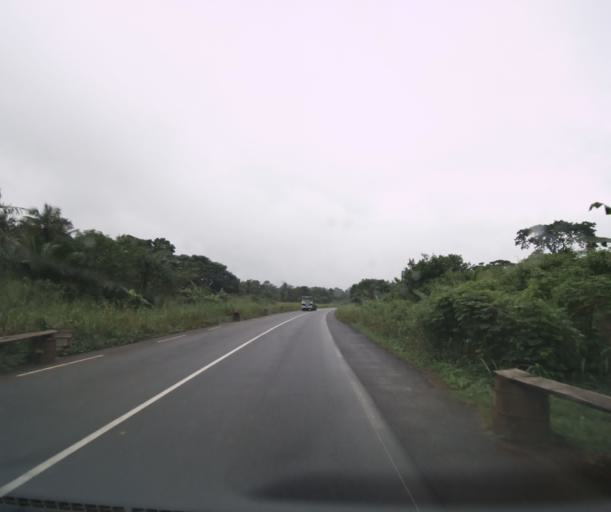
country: CM
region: Littoral
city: Edea
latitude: 3.4753
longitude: 10.1334
